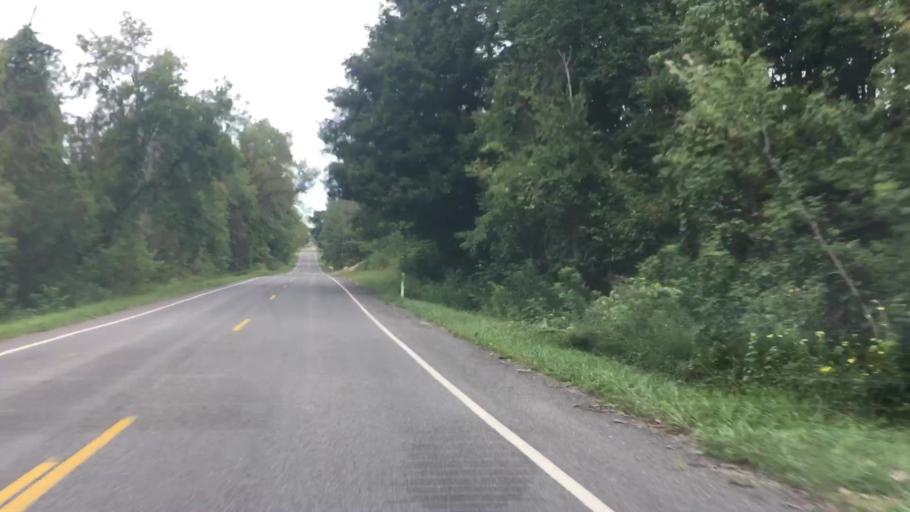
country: US
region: Michigan
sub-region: Kent County
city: Byron Center
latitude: 42.8337
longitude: -85.7826
